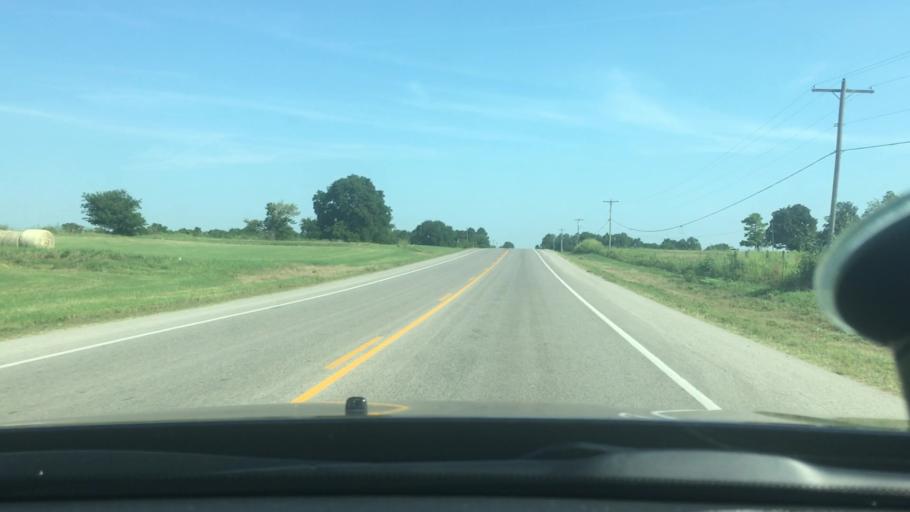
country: US
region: Oklahoma
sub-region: Garvin County
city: Wynnewood
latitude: 34.6600
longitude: -97.2030
